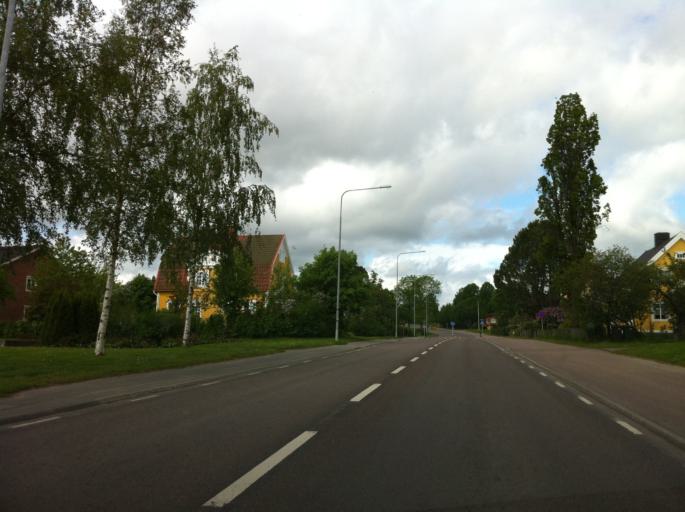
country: SE
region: Vaermland
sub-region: Sunne Kommun
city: Sunne
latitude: 59.8379
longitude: 13.1391
